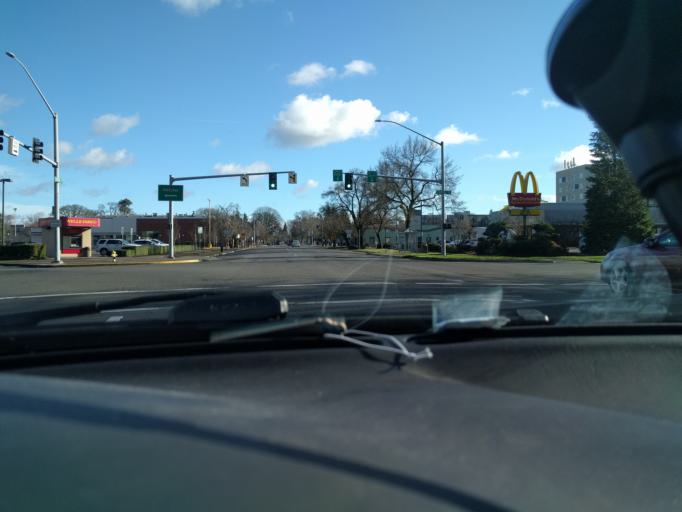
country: US
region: Oregon
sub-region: Marion County
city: Salem
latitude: 44.9410
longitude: -123.0277
